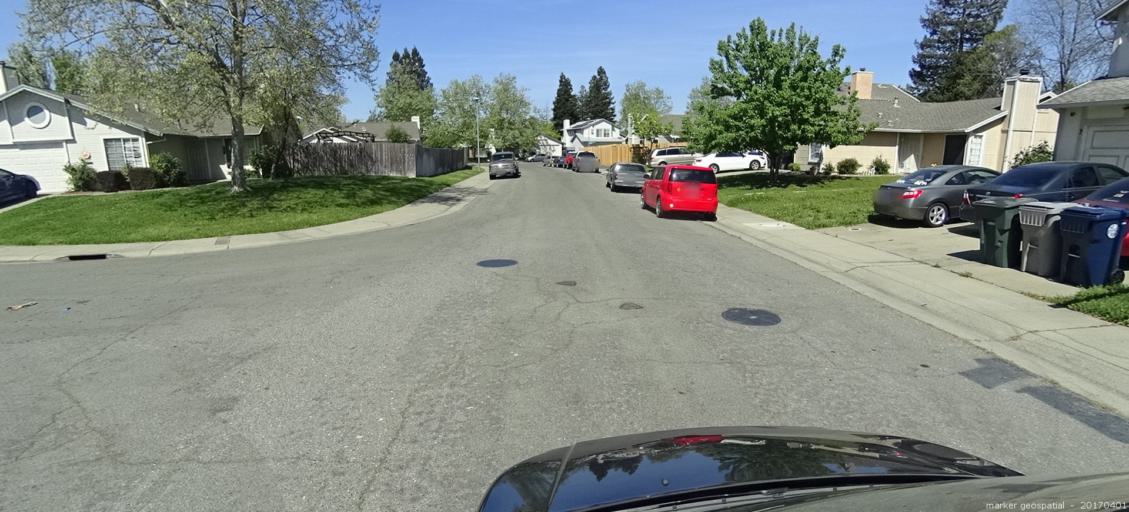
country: US
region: California
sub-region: Sacramento County
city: Laguna
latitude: 38.4476
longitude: -121.4310
